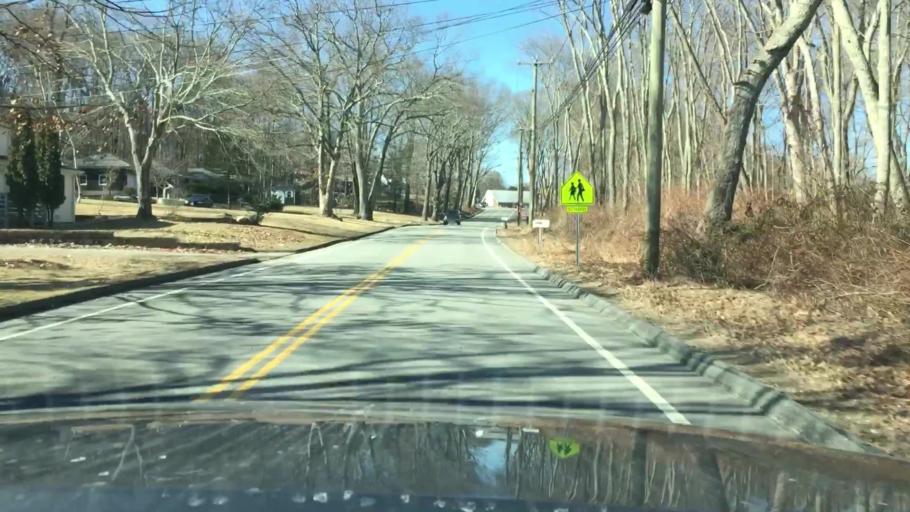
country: US
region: Connecticut
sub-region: New London County
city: Conning Towers-Nautilus Park
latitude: 41.3721
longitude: -72.0644
